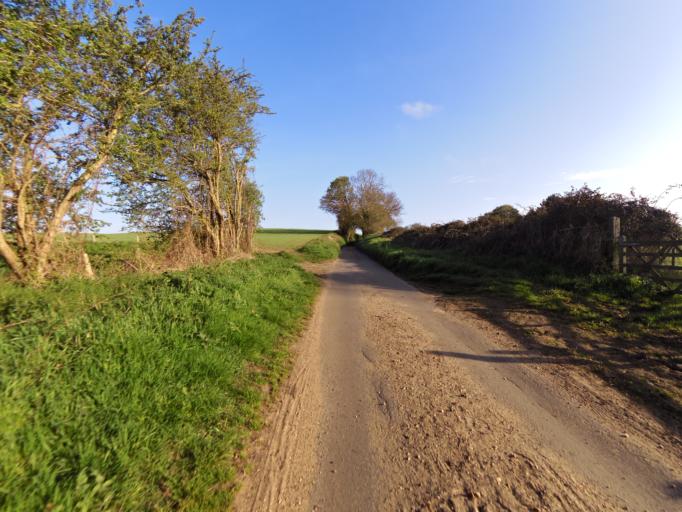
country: GB
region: England
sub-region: Suffolk
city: Bramford
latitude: 52.0421
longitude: 1.0721
